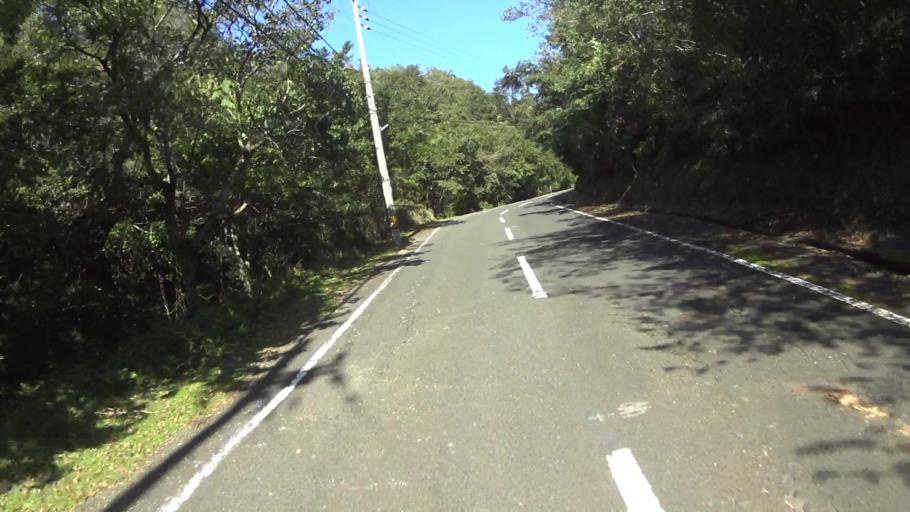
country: JP
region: Hyogo
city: Toyooka
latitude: 35.6421
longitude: 134.8864
